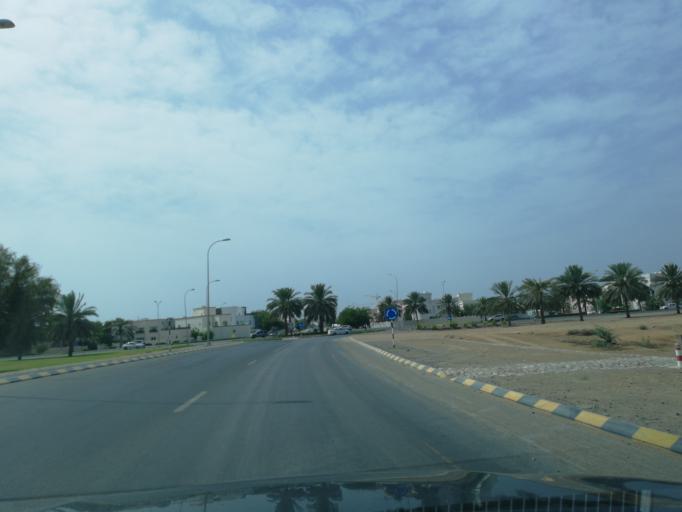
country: OM
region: Muhafazat Masqat
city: As Sib al Jadidah
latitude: 23.6155
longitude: 58.2535
